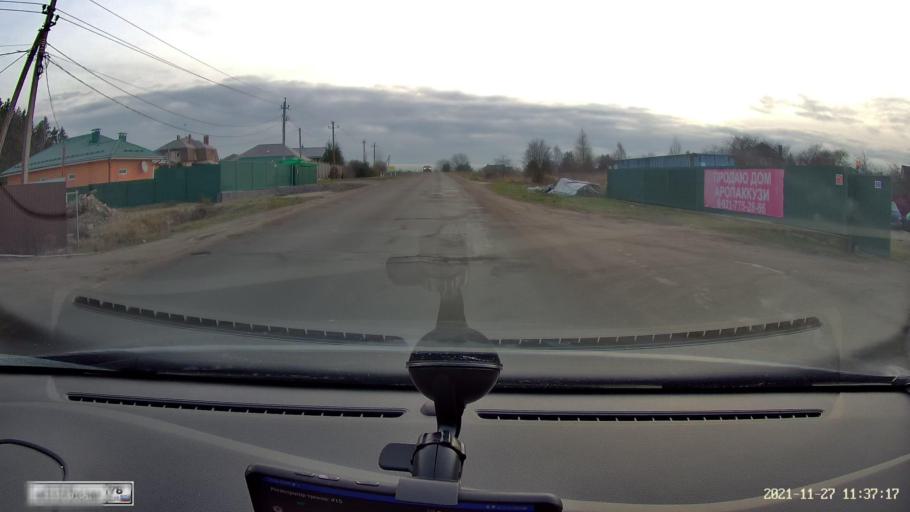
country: RU
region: Leningrad
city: Russko-Vysotskoye
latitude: 59.6948
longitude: 29.9854
